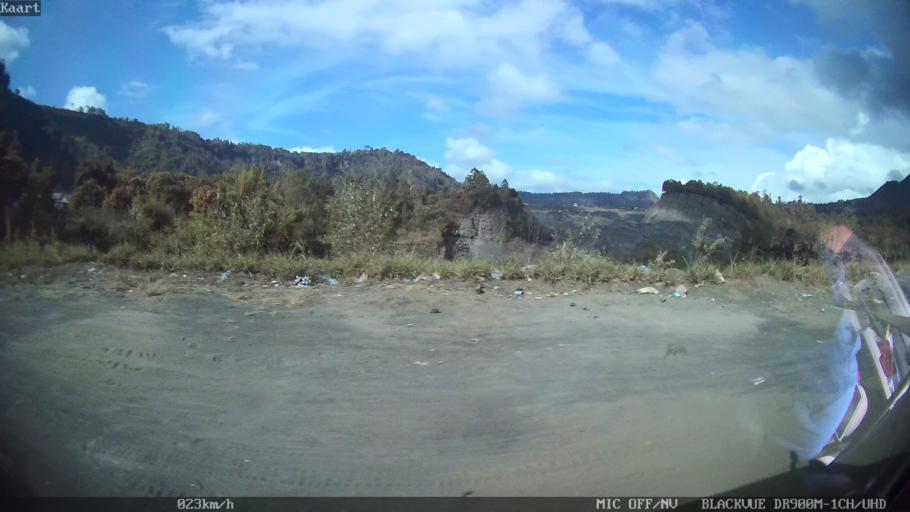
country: ID
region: Bali
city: Banjar Kedisan
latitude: -8.2181
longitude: 115.3644
